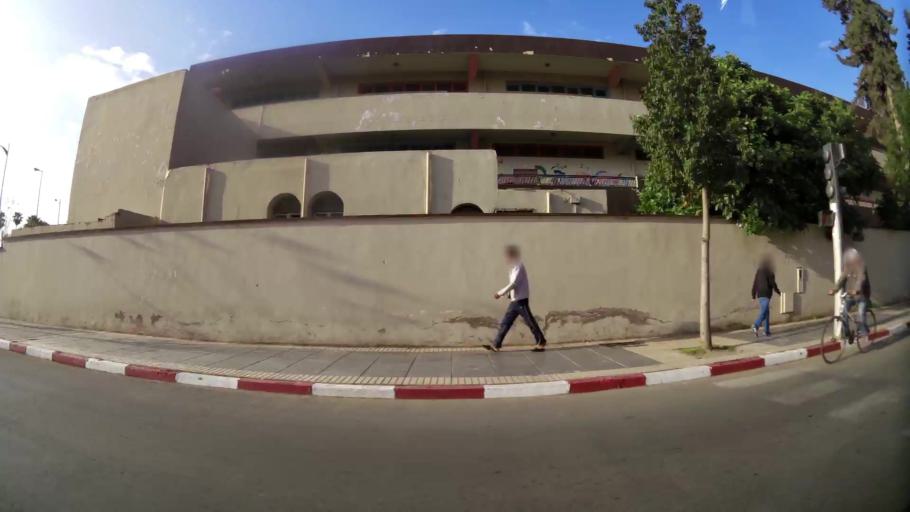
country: MA
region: Oriental
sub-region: Oujda-Angad
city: Oujda
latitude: 34.6772
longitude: -1.9179
